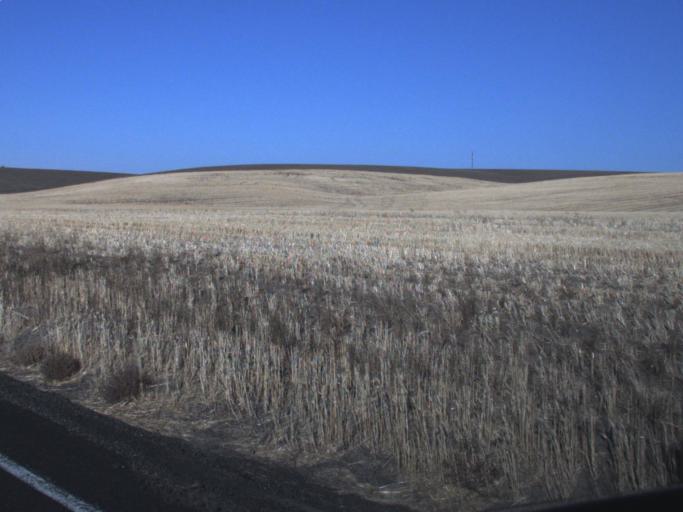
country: US
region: Washington
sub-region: Adams County
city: Ritzville
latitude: 47.0862
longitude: -118.3654
